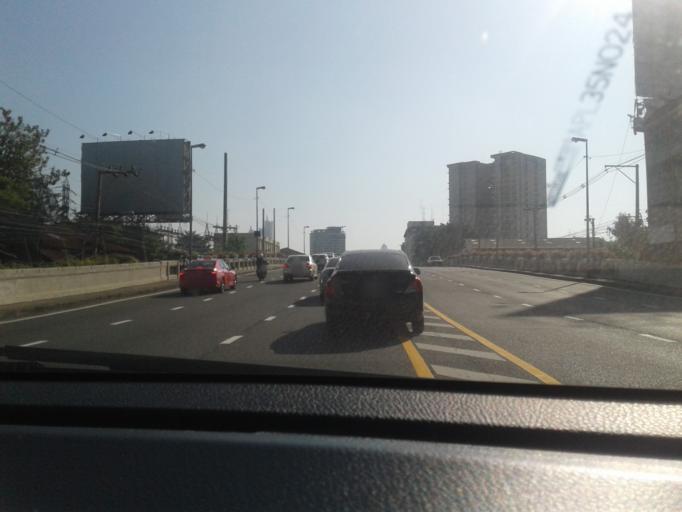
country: TH
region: Bangkok
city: Thon Buri
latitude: 13.7277
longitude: 100.4845
